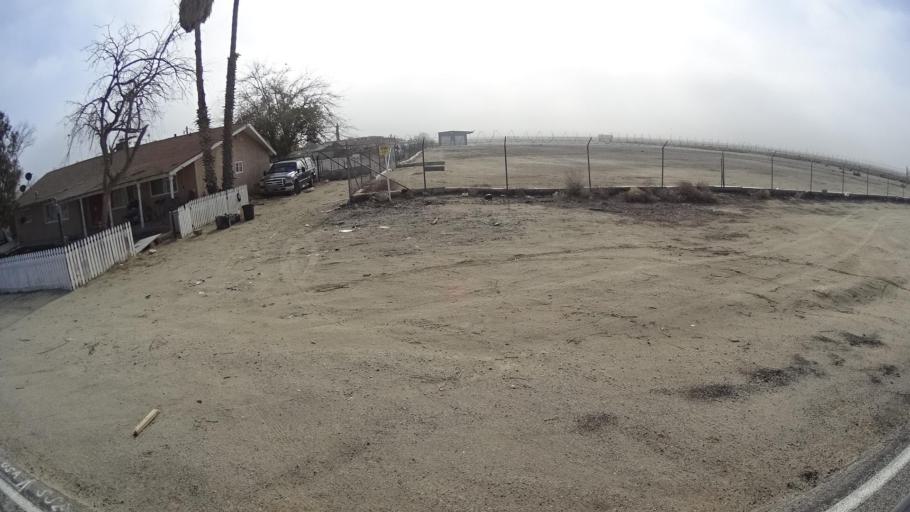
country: US
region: California
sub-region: Kern County
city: Ford City
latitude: 35.2097
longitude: -119.4117
